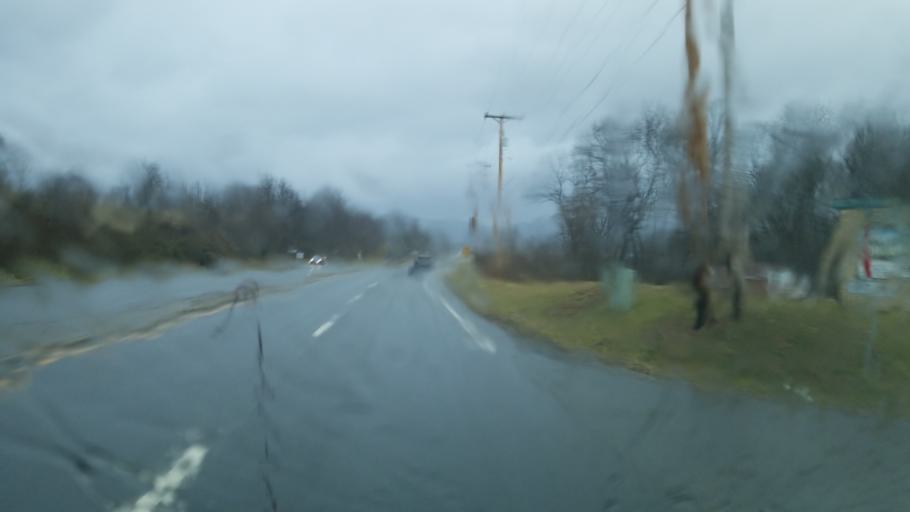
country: US
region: Virginia
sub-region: Giles County
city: Pearisburg
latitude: 37.3165
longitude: -80.7319
